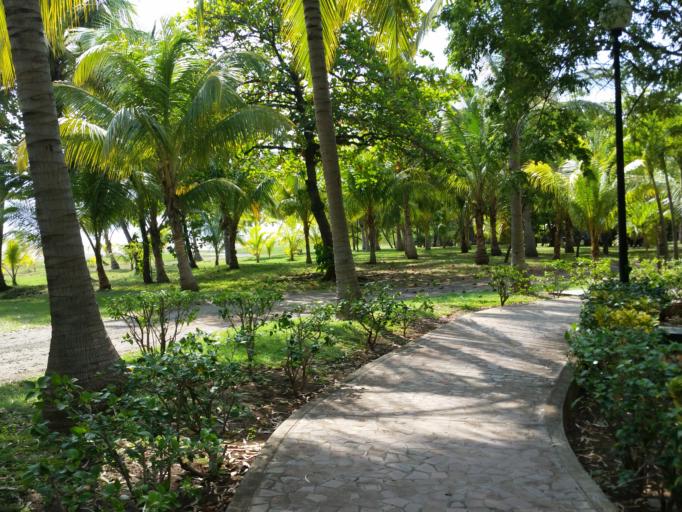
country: NI
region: Managua
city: Masachapa
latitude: 11.8092
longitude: -86.5224
